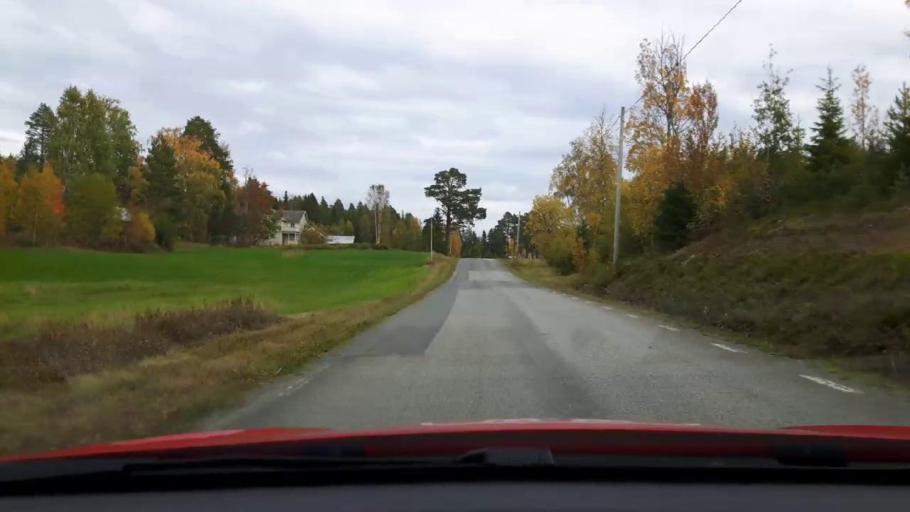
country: SE
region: Jaemtland
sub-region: Krokoms Kommun
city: Valla
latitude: 63.2605
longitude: 14.0054
